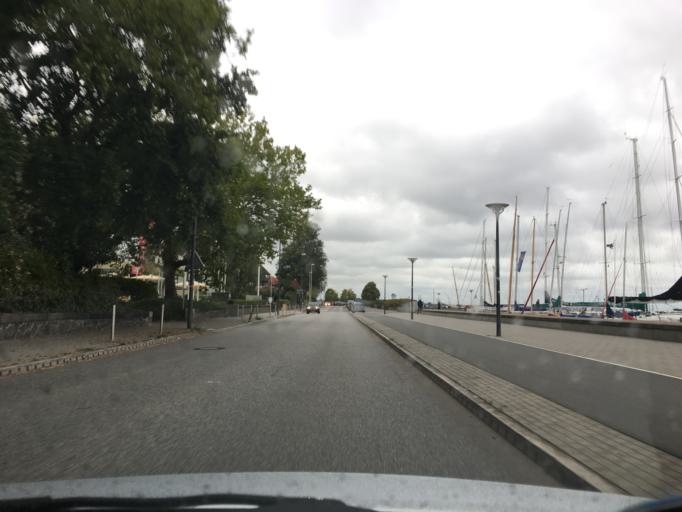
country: DE
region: Schleswig-Holstein
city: Kiel
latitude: 54.3390
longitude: 10.1569
